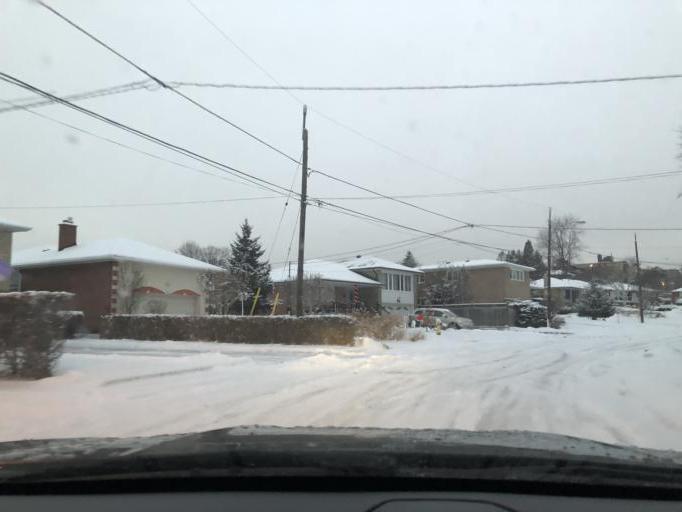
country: CA
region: Ontario
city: Toronto
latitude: 43.6973
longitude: -79.4825
